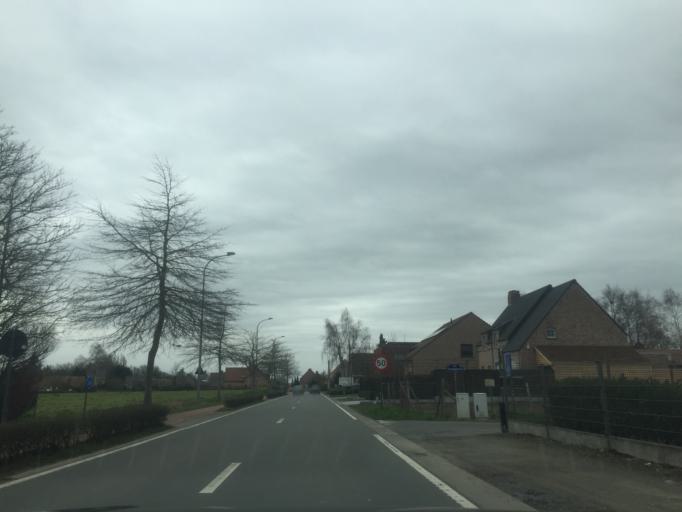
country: BE
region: Flanders
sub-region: Provincie West-Vlaanderen
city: Izegem
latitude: 50.9419
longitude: 3.2049
